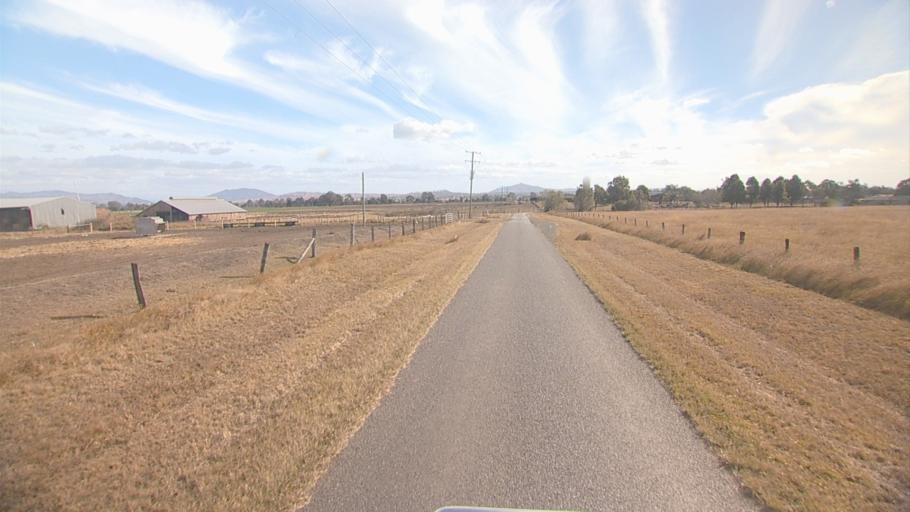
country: AU
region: Queensland
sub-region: Logan
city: Cedar Vale
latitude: -27.9227
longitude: 152.9727
